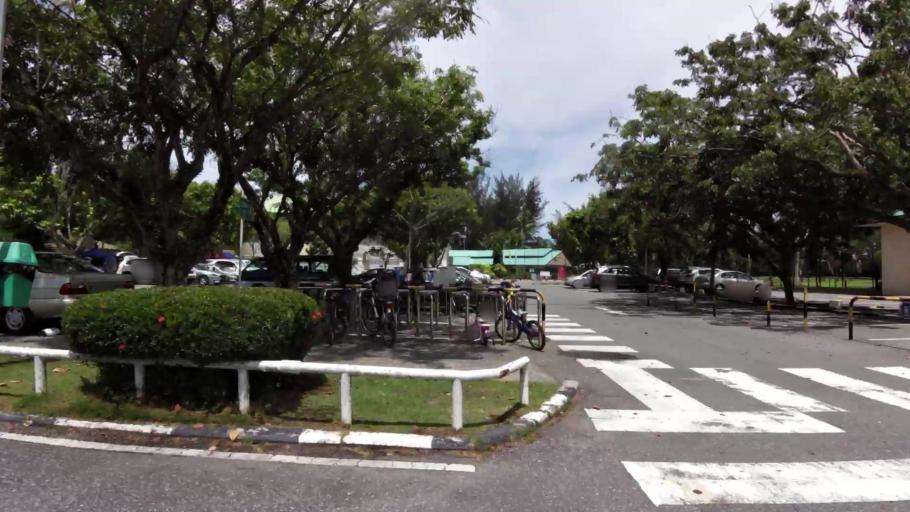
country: BN
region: Belait
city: Kuala Belait
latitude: 4.6011
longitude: 114.2702
